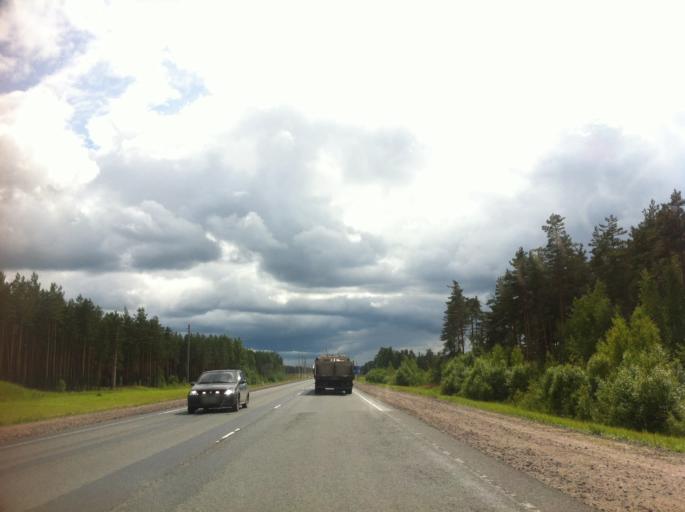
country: RU
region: Leningrad
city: Luga
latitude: 58.7383
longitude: 29.8889
